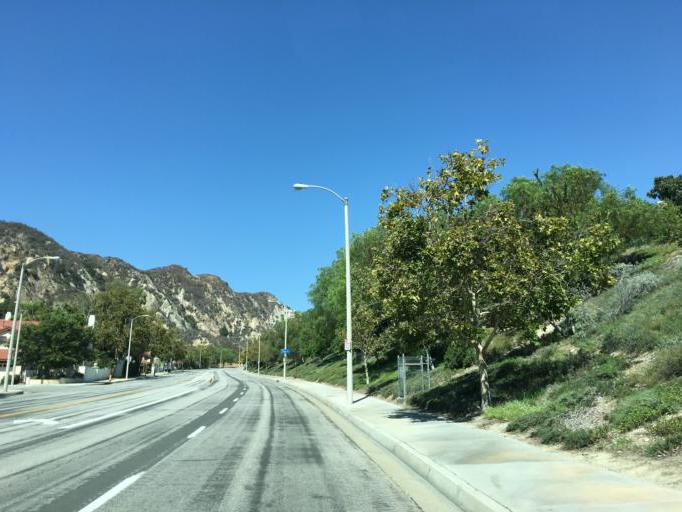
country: US
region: California
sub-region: Los Angeles County
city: Santa Clarita
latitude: 34.3828
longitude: -118.5872
